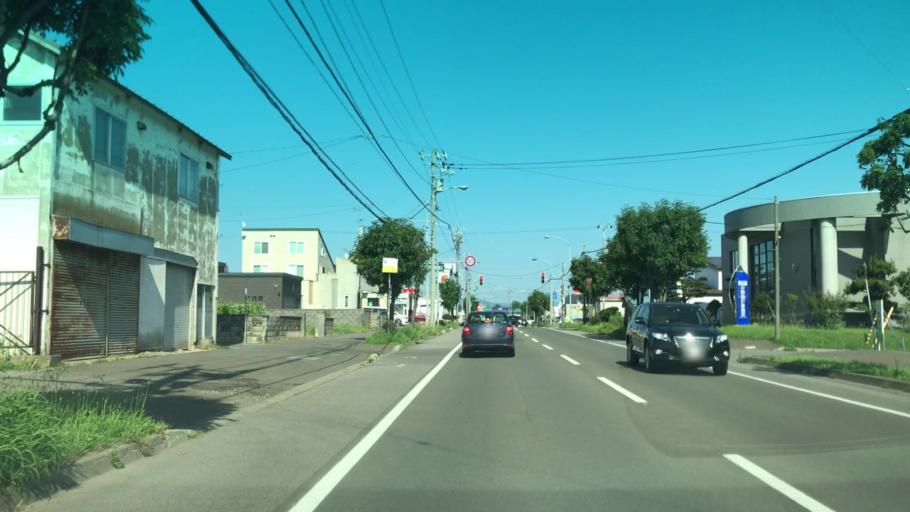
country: JP
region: Hokkaido
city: Iwanai
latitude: 42.9828
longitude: 140.5320
